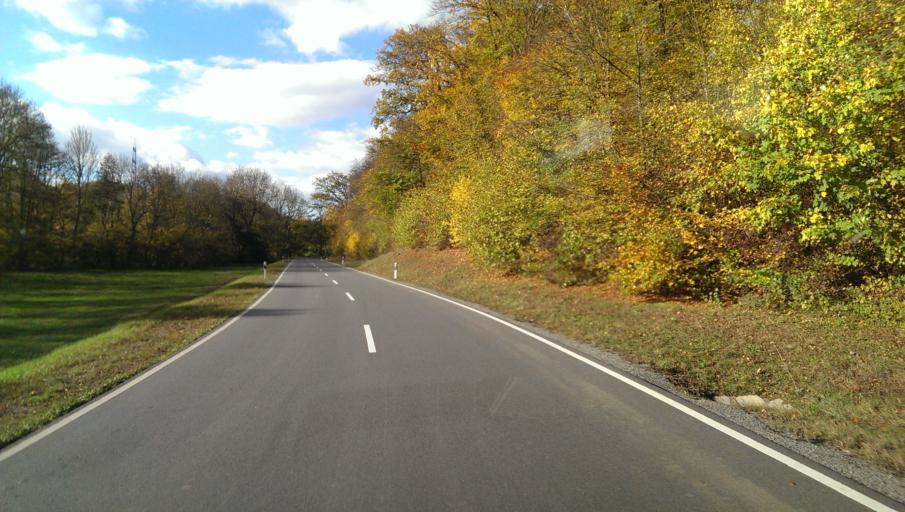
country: DE
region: Baden-Wuerttemberg
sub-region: Karlsruhe Region
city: Seckach
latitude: 49.4736
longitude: 9.3471
